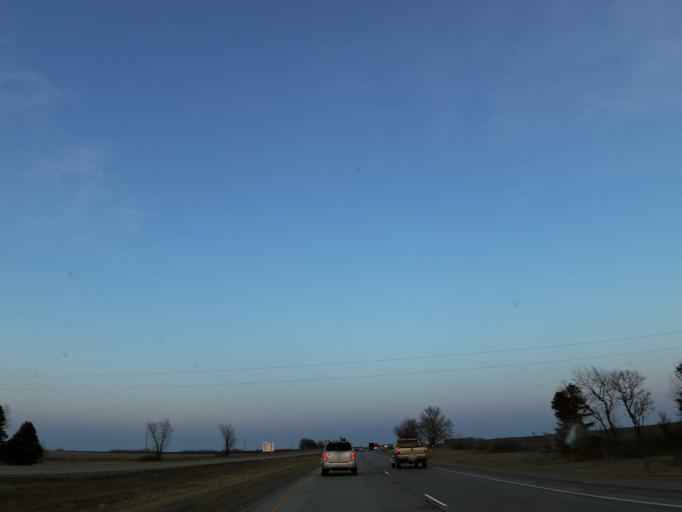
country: US
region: Minnesota
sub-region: Mower County
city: Austin
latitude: 43.6731
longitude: -92.8498
